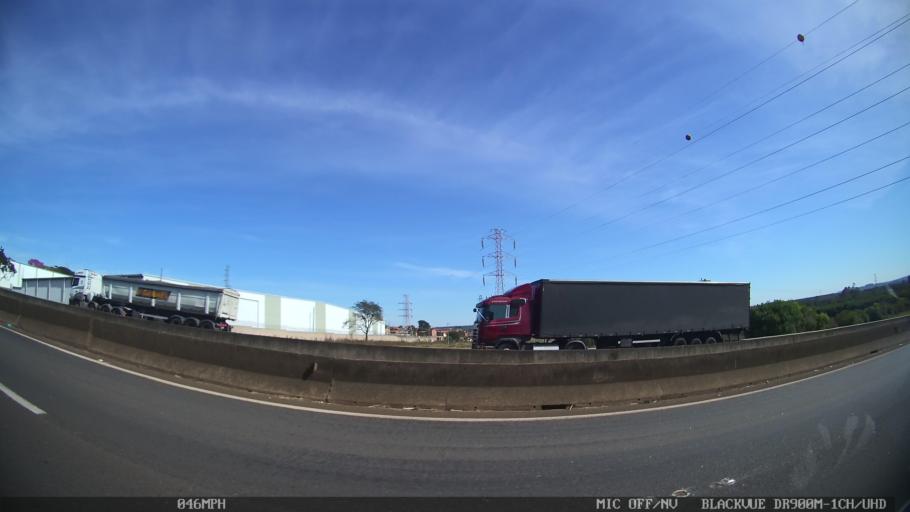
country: BR
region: Sao Paulo
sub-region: Porto Ferreira
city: Porto Ferreira
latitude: -21.8477
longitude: -47.4950
